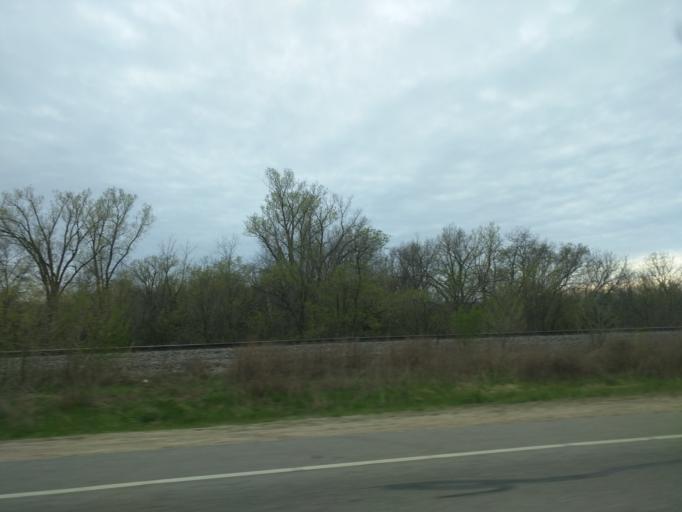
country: US
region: Minnesota
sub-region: Goodhue County
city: Red Wing
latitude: 44.6251
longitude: -92.5785
